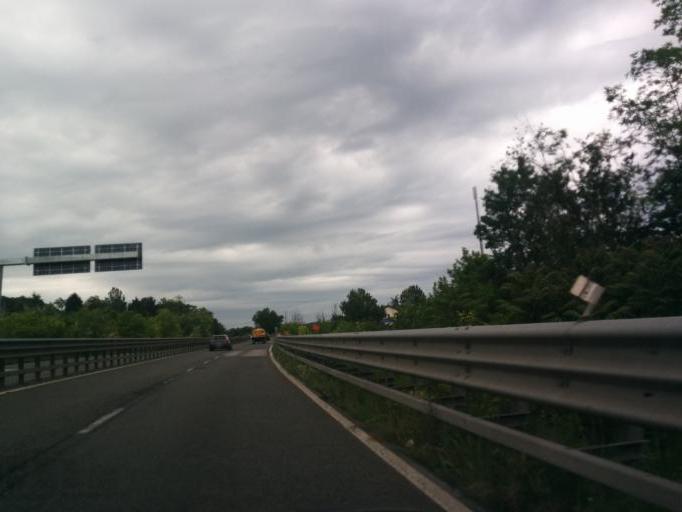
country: IT
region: Tuscany
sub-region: Provincia di Siena
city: Monteriggioni
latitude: 43.3867
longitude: 11.2728
